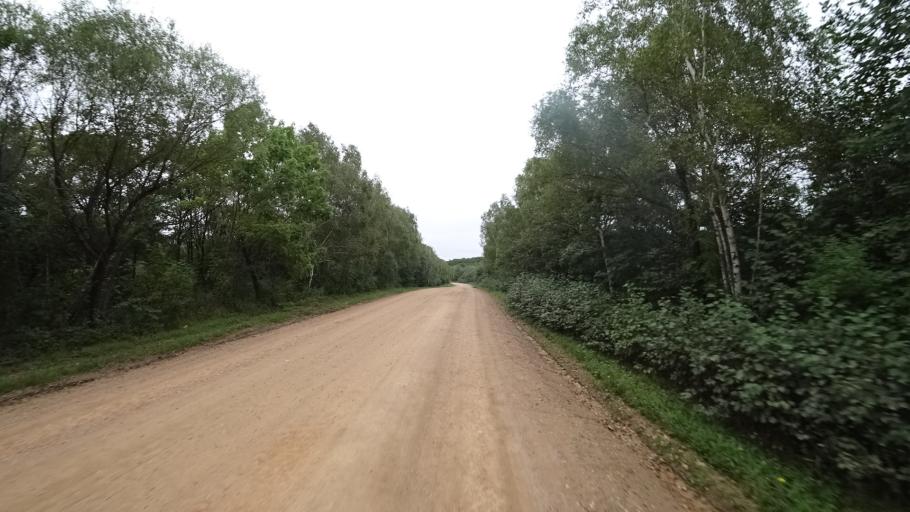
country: RU
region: Primorskiy
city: Rettikhovka
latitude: 44.1746
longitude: 132.7991
